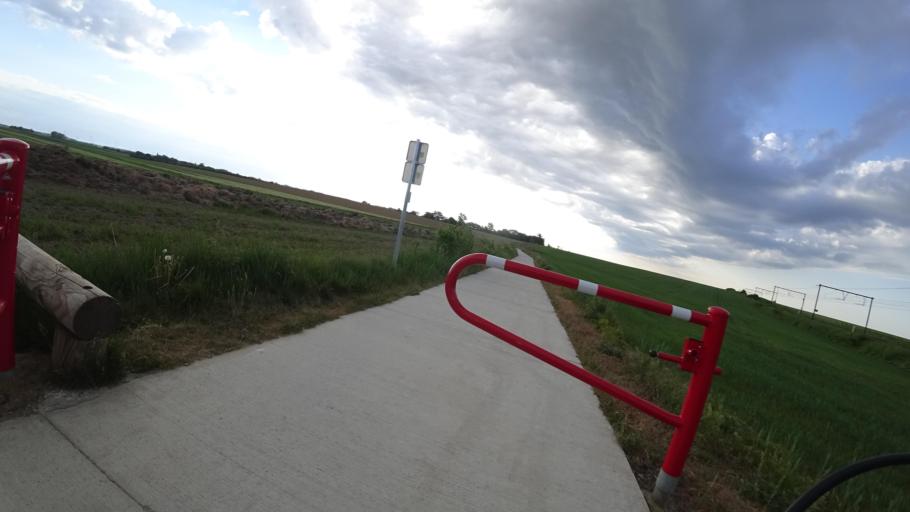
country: BE
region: Wallonia
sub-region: Province de Namur
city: Gembloux
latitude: 50.5589
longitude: 4.7097
